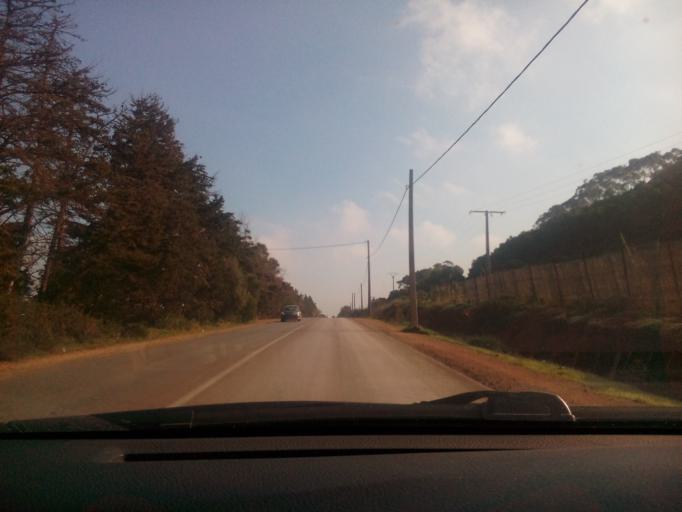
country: DZ
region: Oran
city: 'Ain el Turk
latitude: 35.7041
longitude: -0.8346
